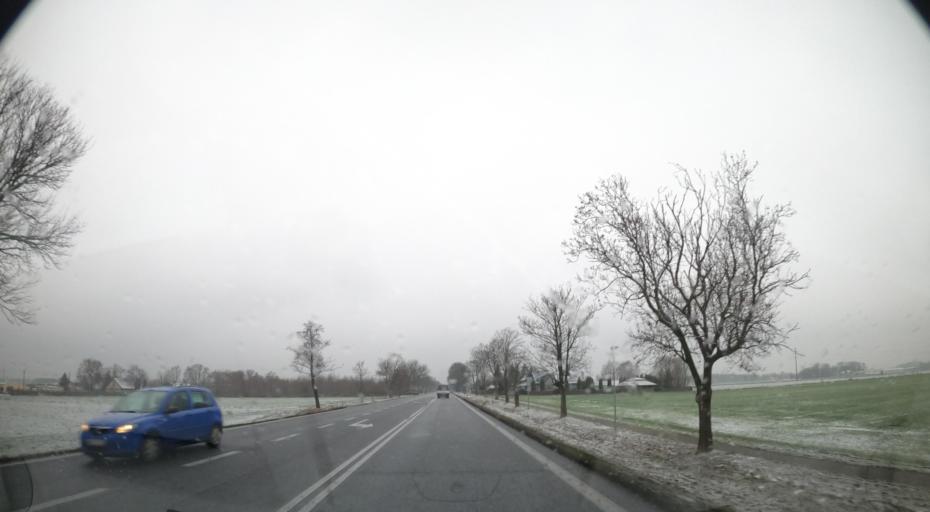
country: PL
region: Masovian Voivodeship
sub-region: Powiat sochaczewski
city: Teresin
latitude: 52.2165
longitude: 20.3808
